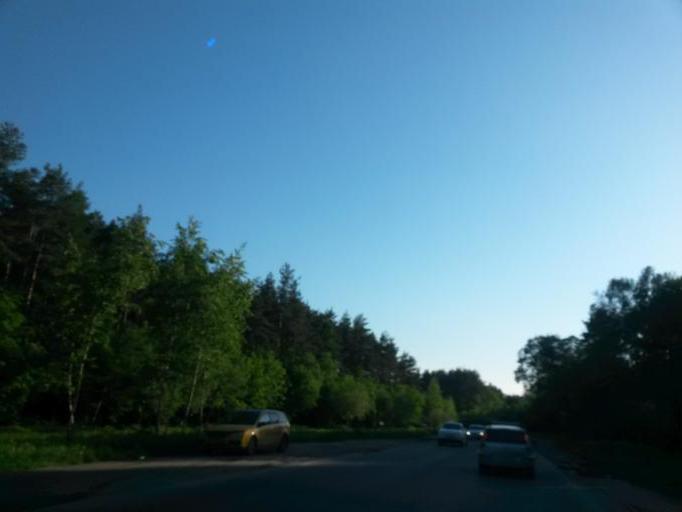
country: RU
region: Moscow
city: Annino
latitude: 55.5560
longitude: 37.5704
